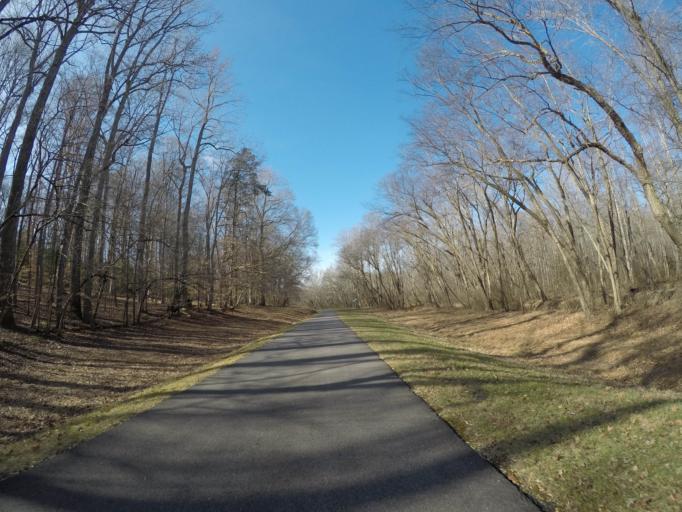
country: US
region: Maryland
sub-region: Charles County
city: Bennsville
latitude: 38.5968
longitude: -77.0038
